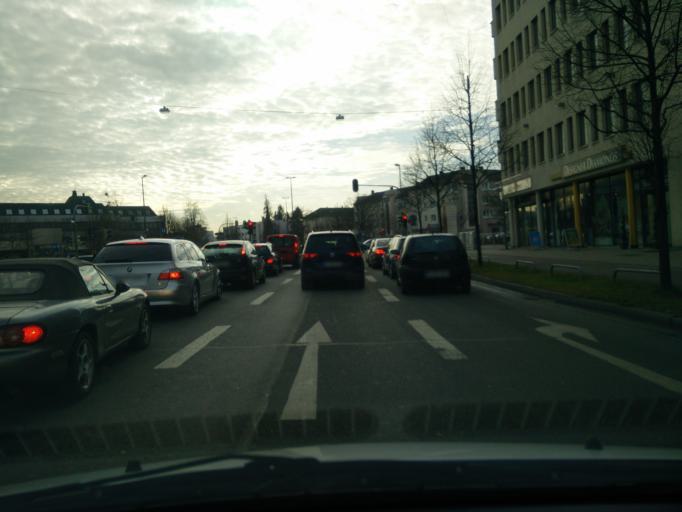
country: DE
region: Bavaria
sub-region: Upper Bavaria
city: Munich
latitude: 48.1826
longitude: 11.5301
